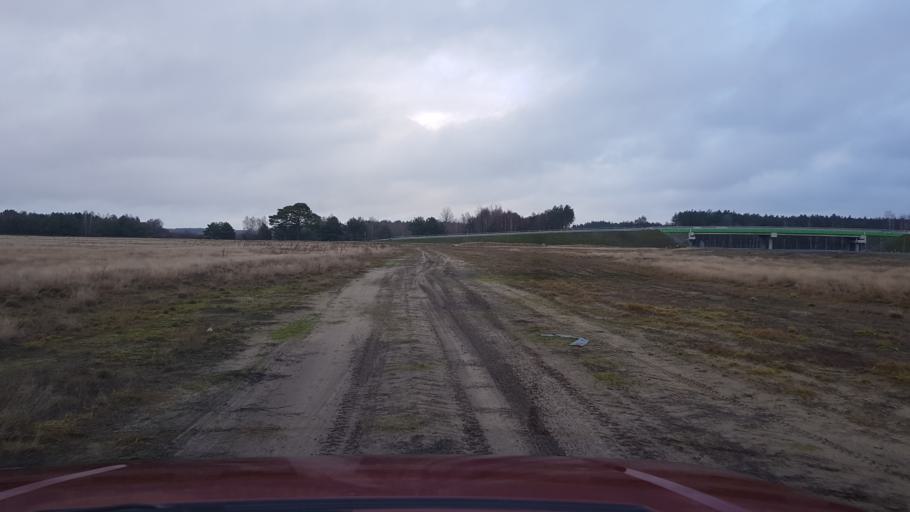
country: PL
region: West Pomeranian Voivodeship
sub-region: Powiat kolobrzeski
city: Kolobrzeg
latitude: 54.1105
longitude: 15.5460
